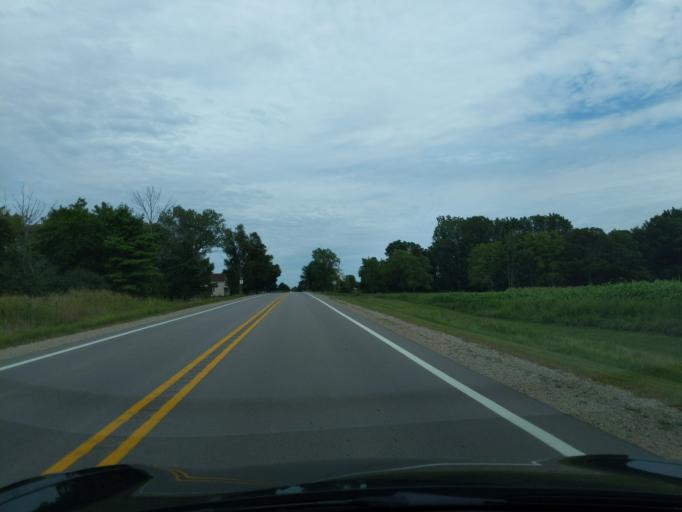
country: US
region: Michigan
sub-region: Barry County
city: Nashville
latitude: 42.5673
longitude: -85.0700
